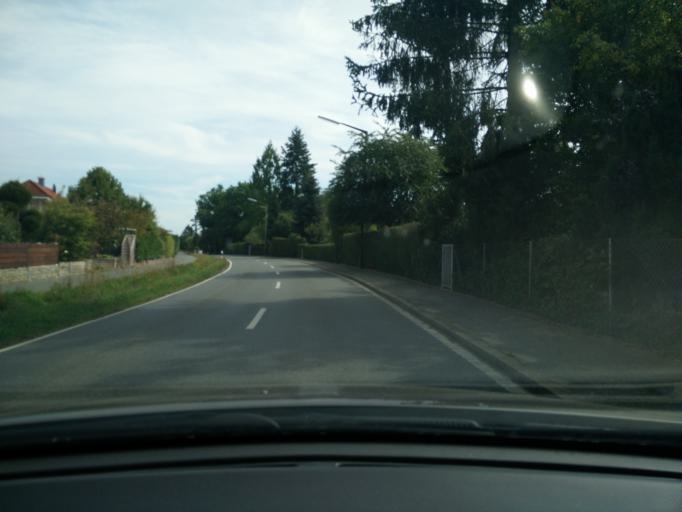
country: DE
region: Bavaria
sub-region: Regierungsbezirk Mittelfranken
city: Veitsbronn
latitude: 49.5131
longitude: 10.8727
